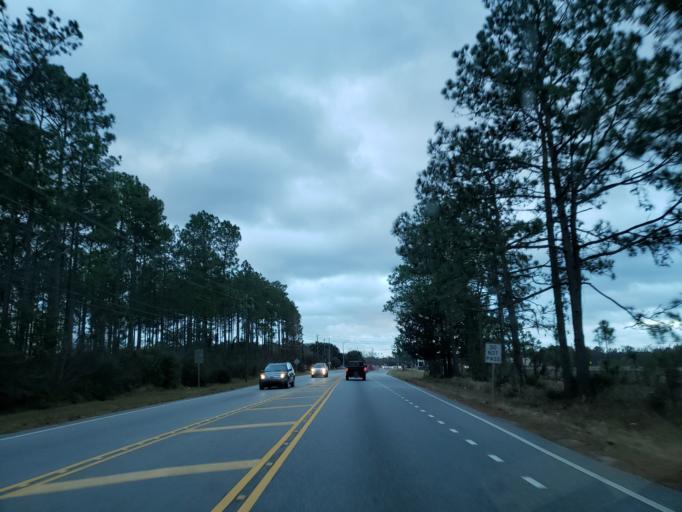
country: US
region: Alabama
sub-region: Mobile County
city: Chickasaw
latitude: 30.7851
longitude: -88.2787
